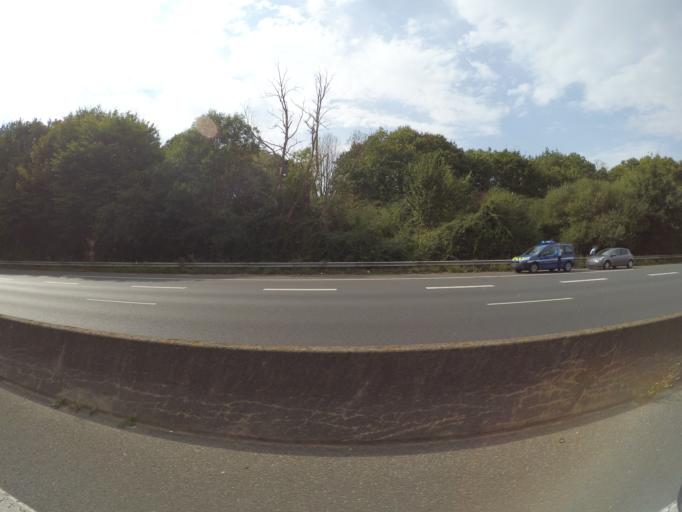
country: FR
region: Pays de la Loire
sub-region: Departement de la Loire-Atlantique
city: Les Sorinieres
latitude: 47.1591
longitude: -1.5130
